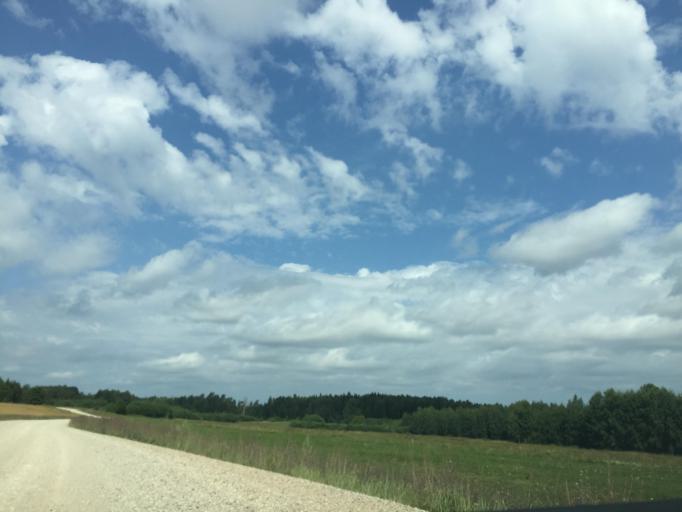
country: LV
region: Kandava
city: Kandava
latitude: 57.0035
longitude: 22.8539
